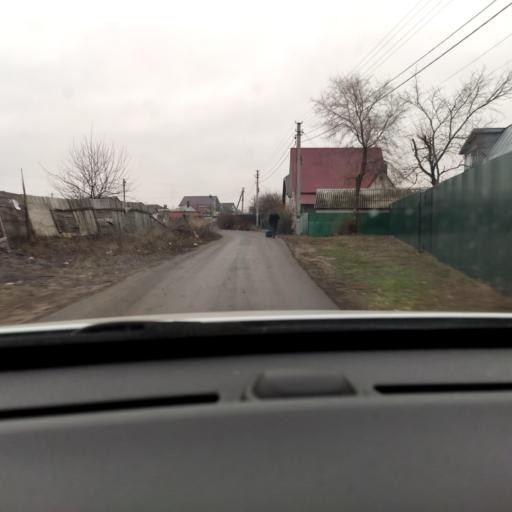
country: RU
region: Voronezj
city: Somovo
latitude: 51.6881
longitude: 39.3612
